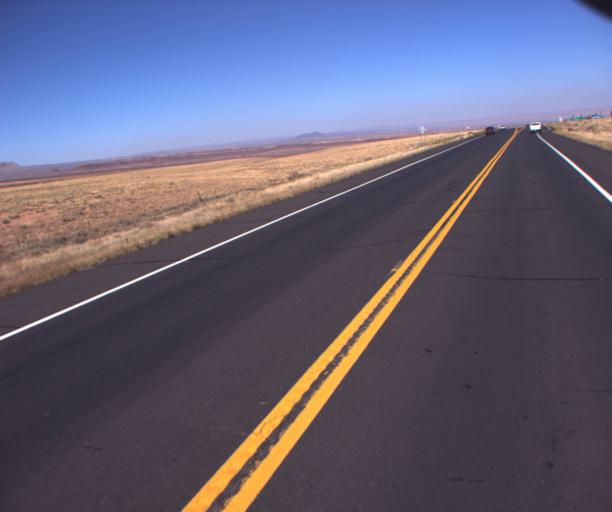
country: US
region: Arizona
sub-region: Coconino County
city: Tuba City
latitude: 35.7498
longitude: -111.4716
